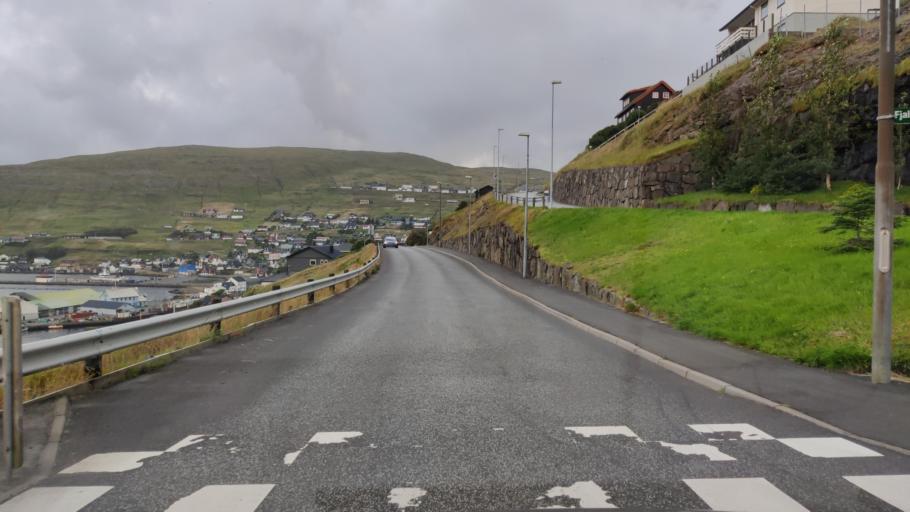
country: FO
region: Streymoy
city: Vestmanna
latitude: 62.1551
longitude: -7.1579
